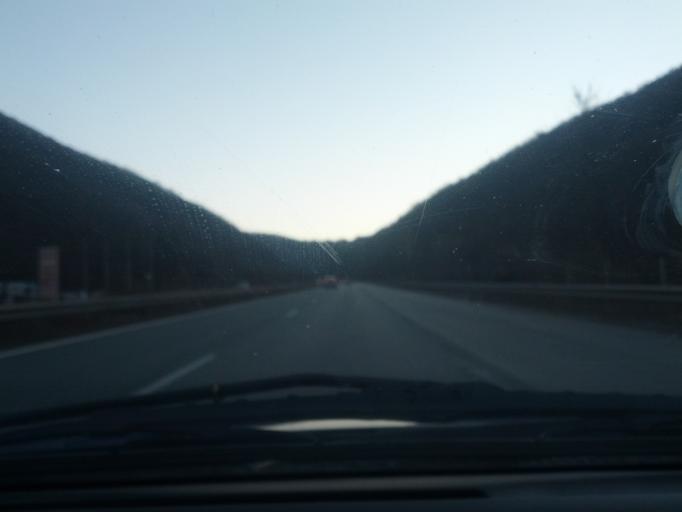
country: BG
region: Sofiya
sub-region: Obshtina Botevgrad
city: Botevgrad
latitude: 42.8741
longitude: 23.8000
